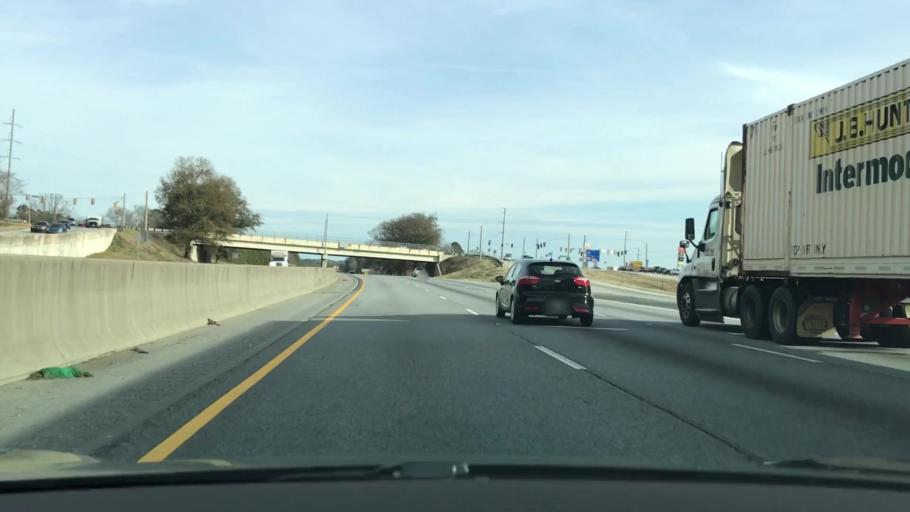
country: US
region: Georgia
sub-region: Newton County
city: Porterdale
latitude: 33.6163
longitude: -83.9230
